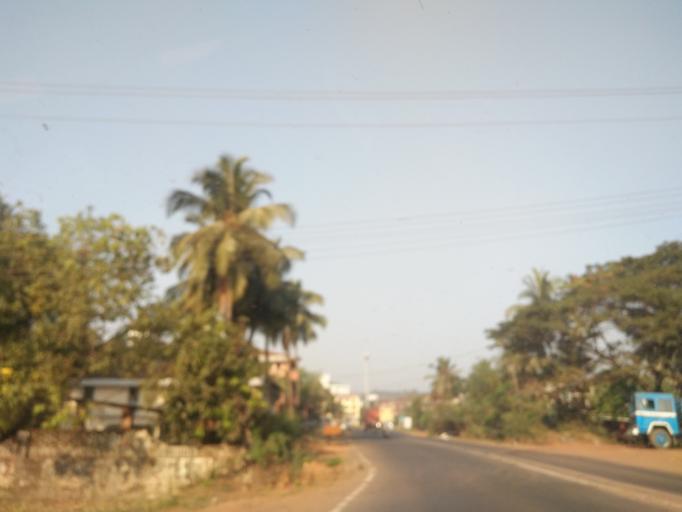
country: IN
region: Goa
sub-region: South Goa
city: Davorlim
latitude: 15.2714
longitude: 73.9805
